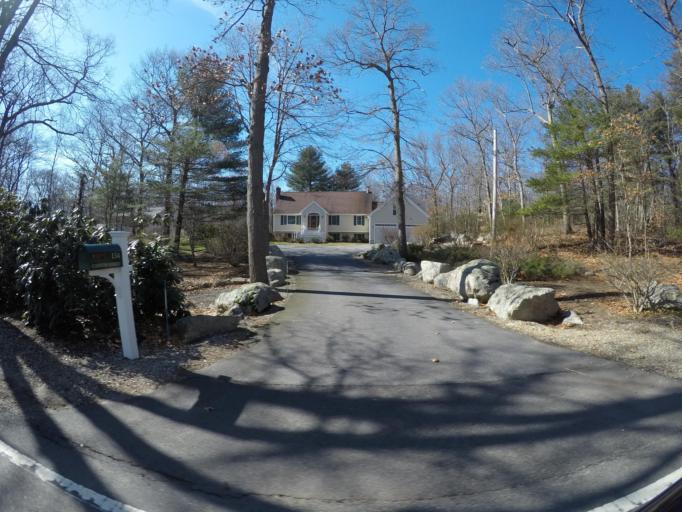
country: US
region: Massachusetts
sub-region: Norfolk County
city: Stoughton
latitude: 42.0802
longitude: -71.1173
